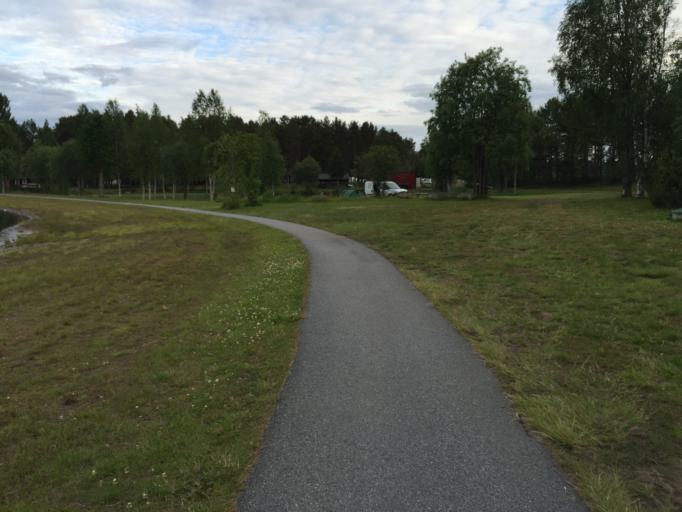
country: SE
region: Vaesterbotten
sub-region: Storumans Kommun
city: Storuman
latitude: 65.1020
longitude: 17.1111
